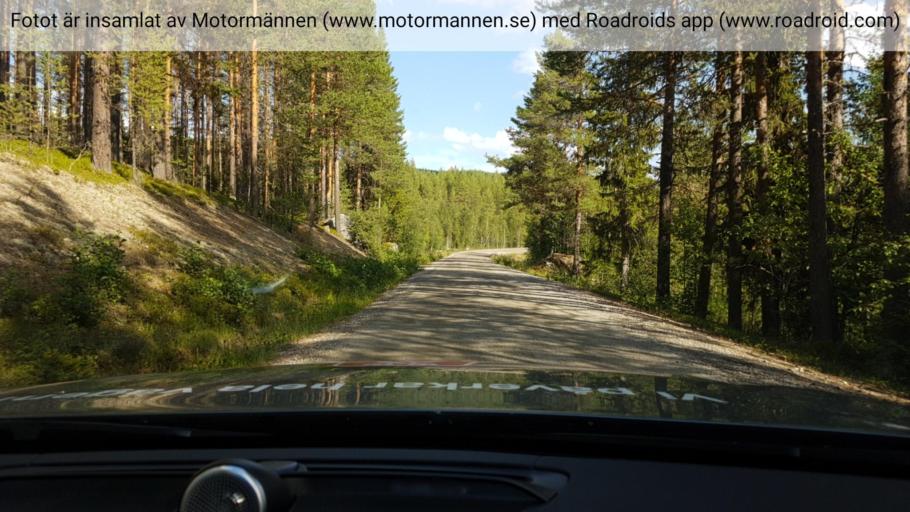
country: SE
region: Vaesterbotten
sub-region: Dorotea Kommun
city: Dorotea
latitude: 63.9739
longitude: 16.0548
